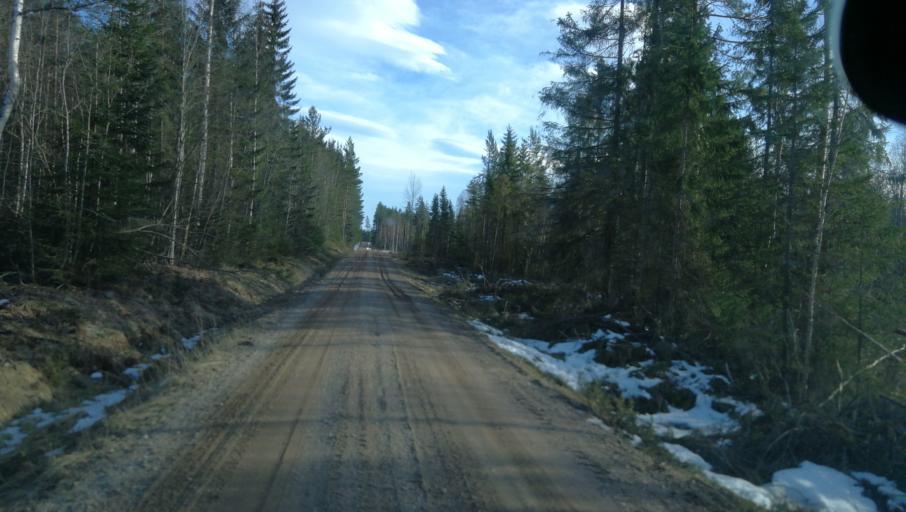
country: SE
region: Dalarna
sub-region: Vansbro Kommun
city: Vansbro
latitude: 60.8148
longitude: 14.2007
